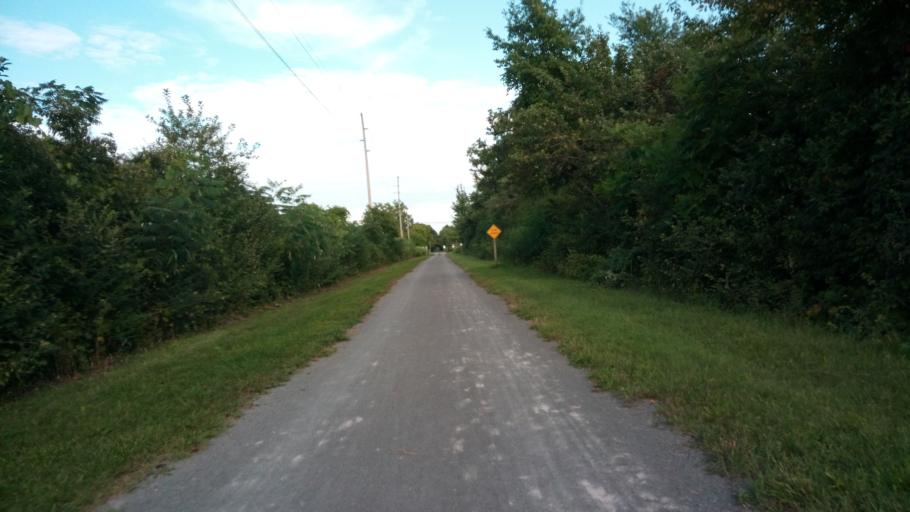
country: US
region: New York
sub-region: Ontario County
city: Victor
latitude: 43.0020
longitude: -77.4718
